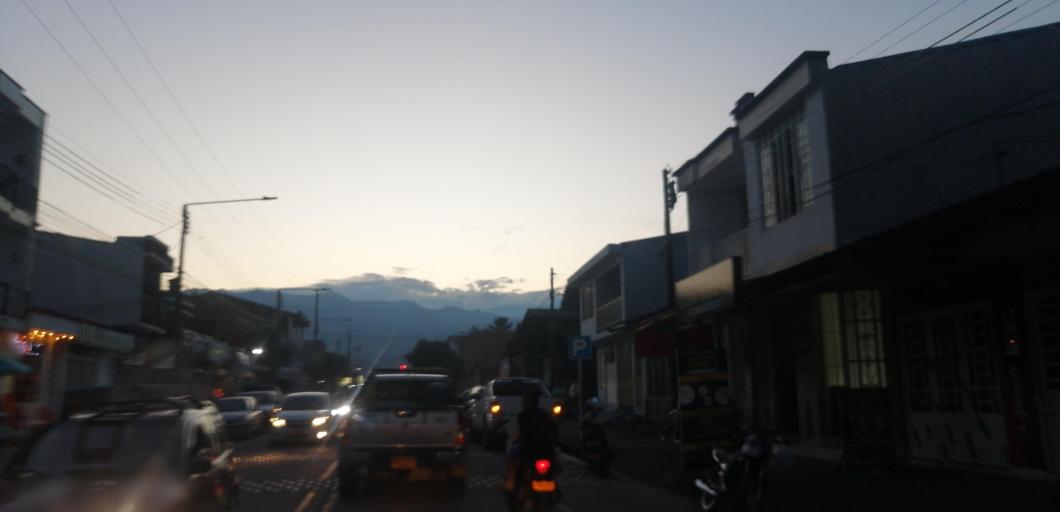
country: CO
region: Meta
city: Acacias
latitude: 3.9879
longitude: -73.7715
